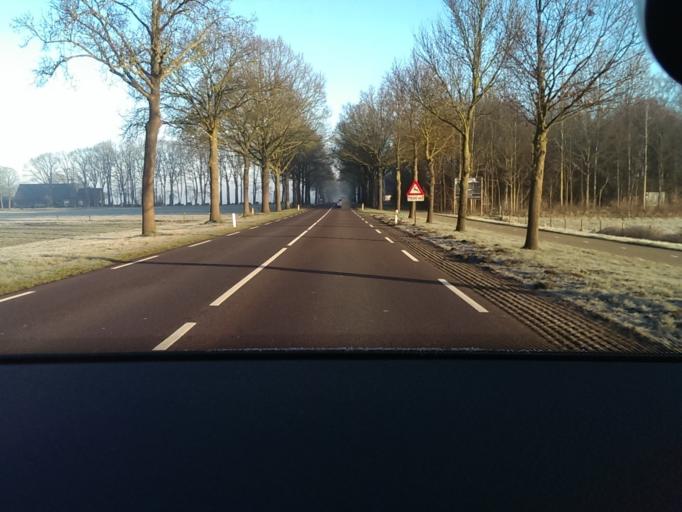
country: NL
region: Overijssel
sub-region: Gemeente Twenterand
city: Vroomshoop
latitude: 52.4112
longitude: 6.5557
